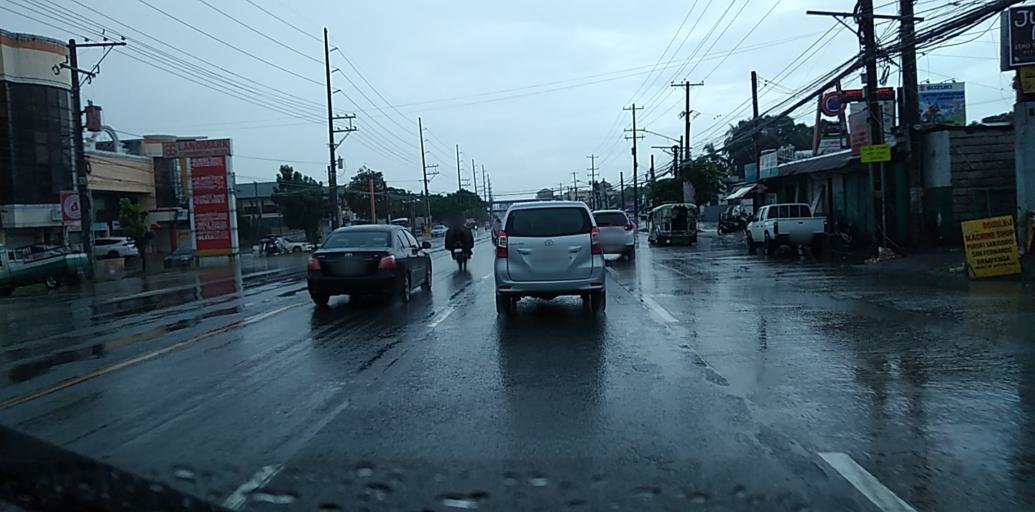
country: PH
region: Central Luzon
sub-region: Province of Pampanga
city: Magliman
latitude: 15.0551
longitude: 120.6605
